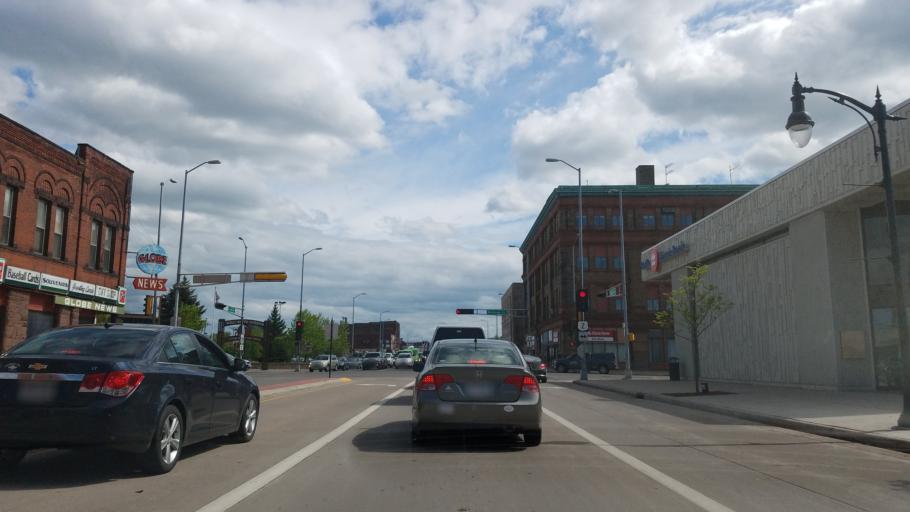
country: US
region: Wisconsin
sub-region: Douglas County
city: Superior
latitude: 46.7213
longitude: -92.1040
